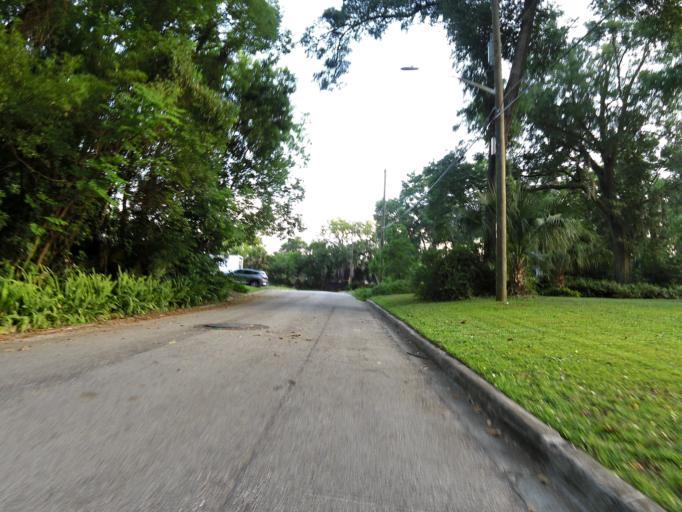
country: US
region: Florida
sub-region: Duval County
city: Jacksonville
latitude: 30.3005
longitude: -81.6311
